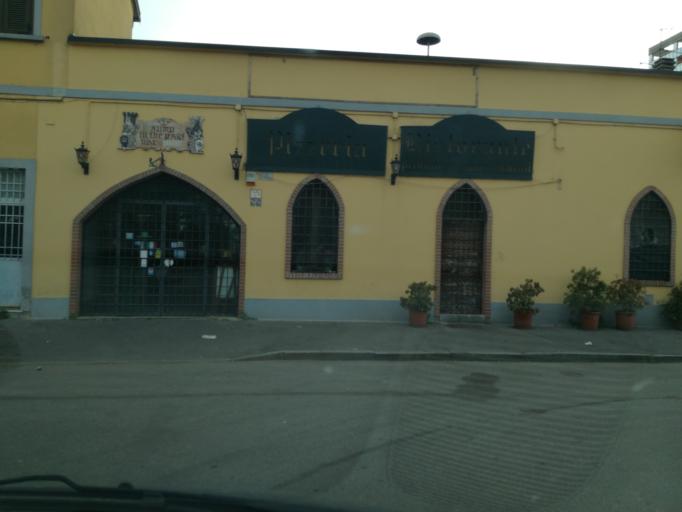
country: IT
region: Lombardy
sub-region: Citta metropolitana di Milano
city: Noverasco-Sporting Mirasole
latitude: 45.4216
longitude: 9.2043
